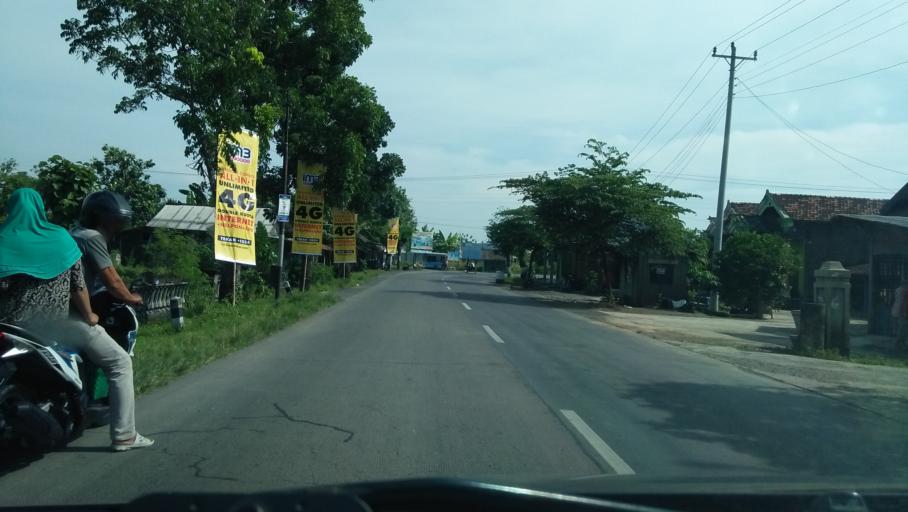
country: ID
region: Central Java
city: Welahan
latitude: -6.8547
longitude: 110.7063
